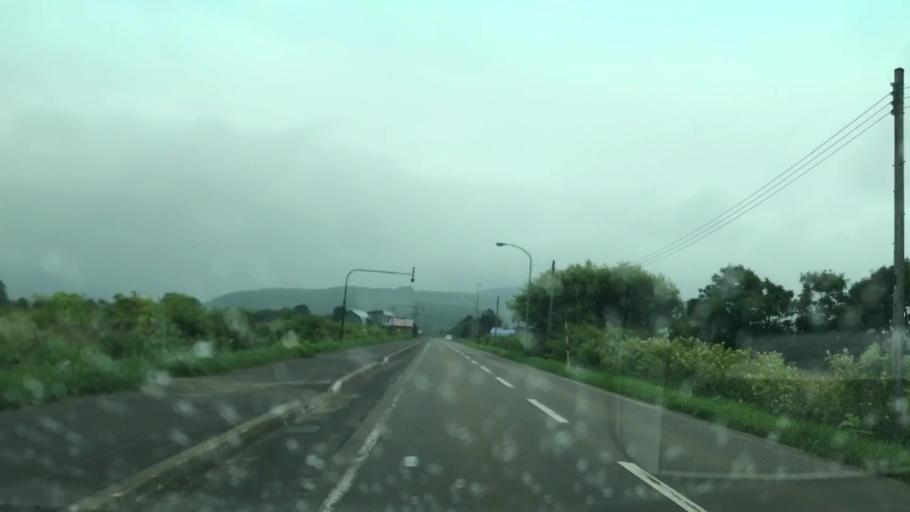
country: JP
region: Hokkaido
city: Iwanai
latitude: 42.7561
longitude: 140.2776
